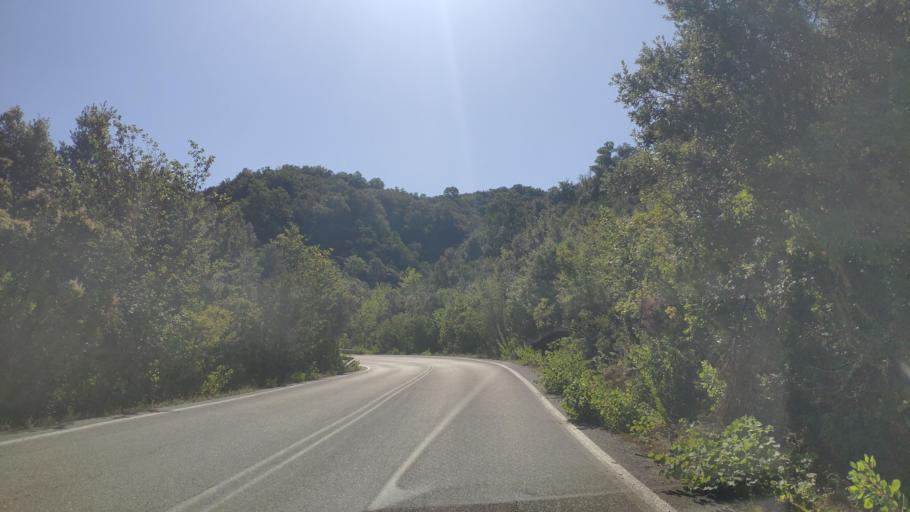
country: GR
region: West Greece
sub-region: Nomos Aitolias kai Akarnanias
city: Sardinia
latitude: 38.9210
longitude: 21.3988
